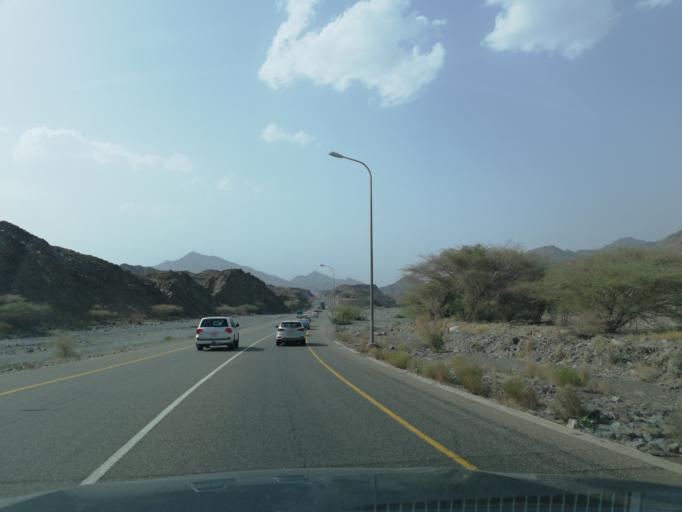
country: OM
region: Muhafazat ad Dakhiliyah
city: Sufalat Sama'il
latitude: 23.2007
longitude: 58.0826
